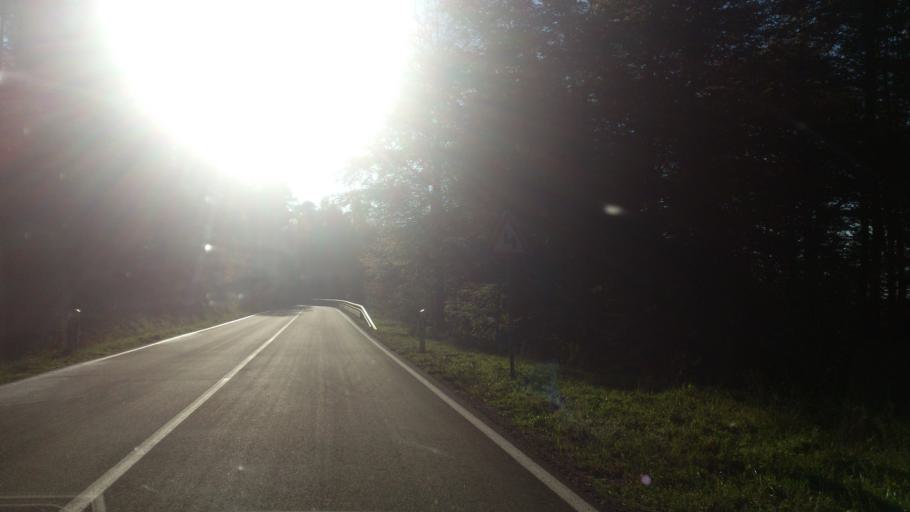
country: DE
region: Rheinland-Pfalz
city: Leimen
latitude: 49.2988
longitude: 7.8377
